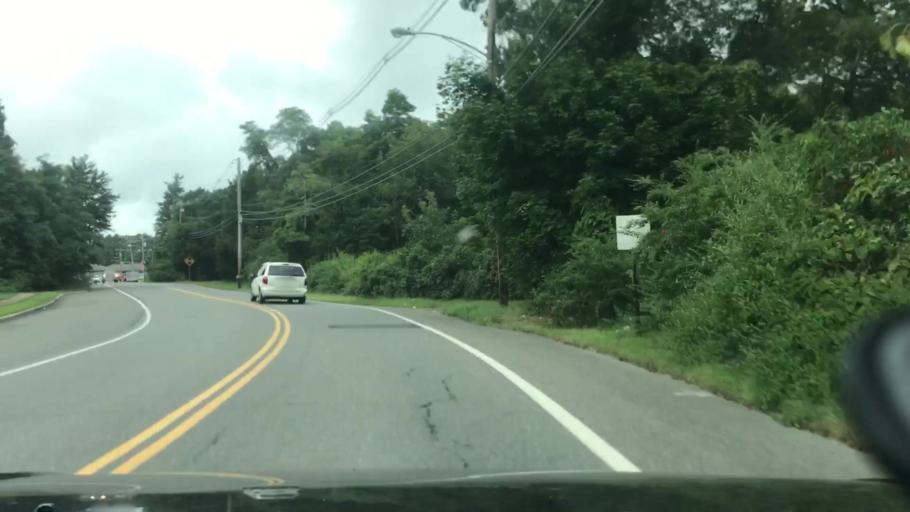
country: US
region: New Jersey
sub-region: Ocean County
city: Barnegat
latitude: 39.7541
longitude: -74.2383
